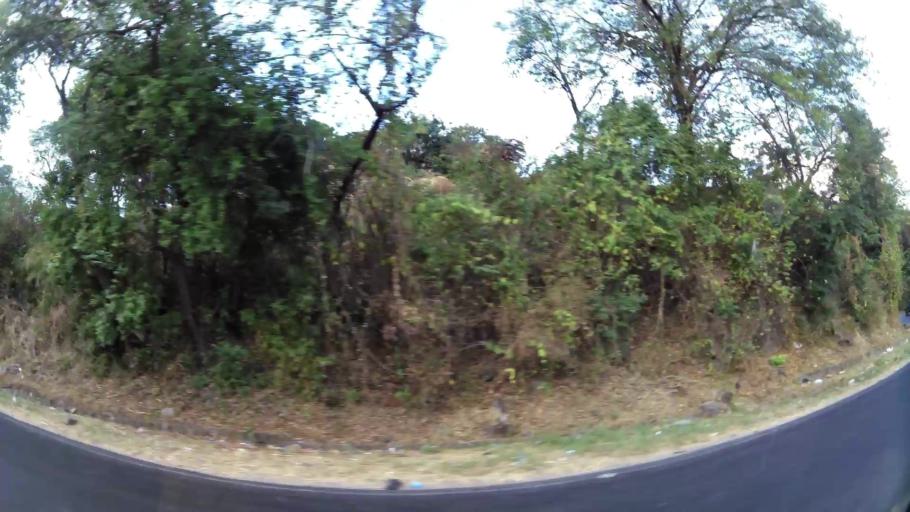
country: SV
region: San Vicente
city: Apastepeque
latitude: 13.6573
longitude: -88.7928
